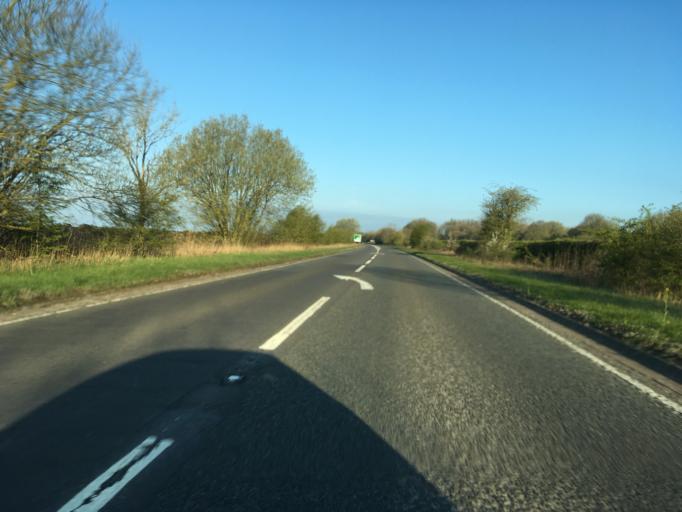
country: GB
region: England
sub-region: Gloucestershire
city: Northleach
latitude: 51.8434
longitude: -1.8536
